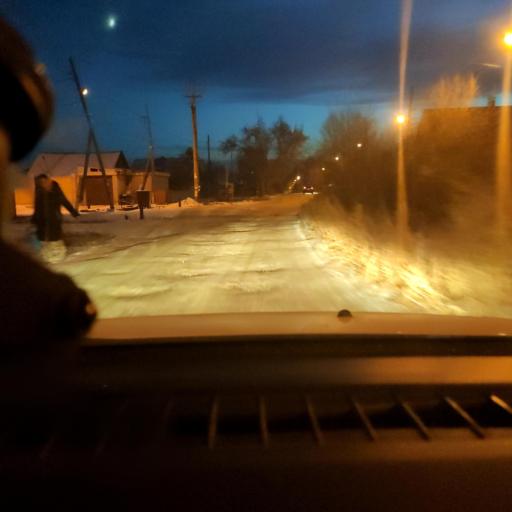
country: RU
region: Samara
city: Petra-Dubrava
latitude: 53.2558
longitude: 50.3340
